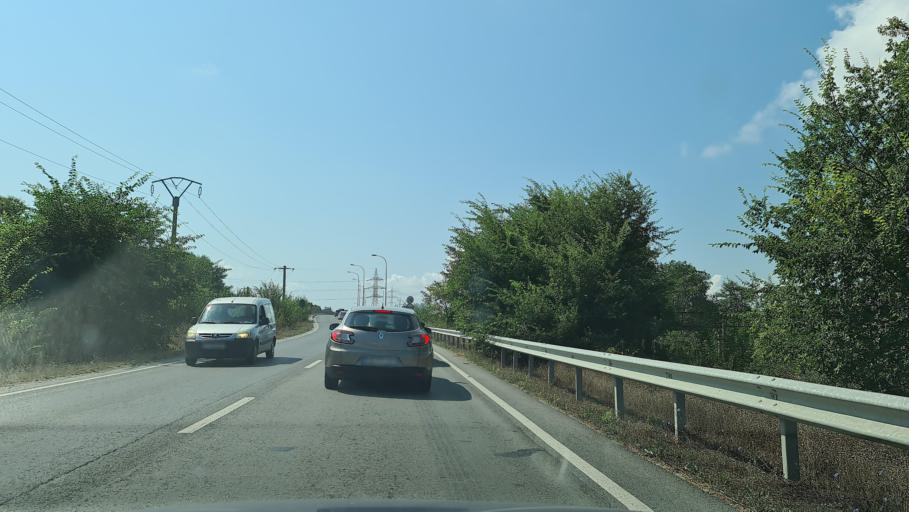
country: RO
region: Constanta
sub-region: Comuna Agigea
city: Agigea
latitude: 44.0882
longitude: 28.6401
